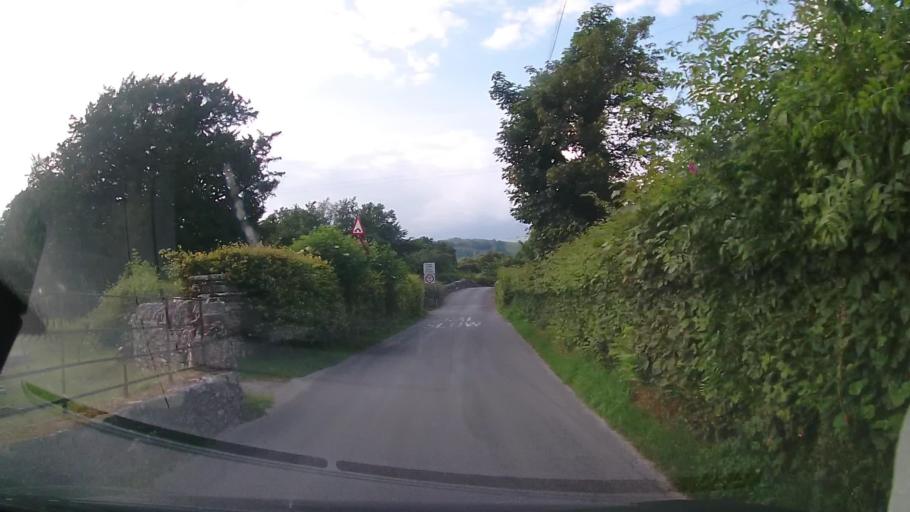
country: GB
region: Wales
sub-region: Gwynedd
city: Bala
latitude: 52.8767
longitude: -3.6295
